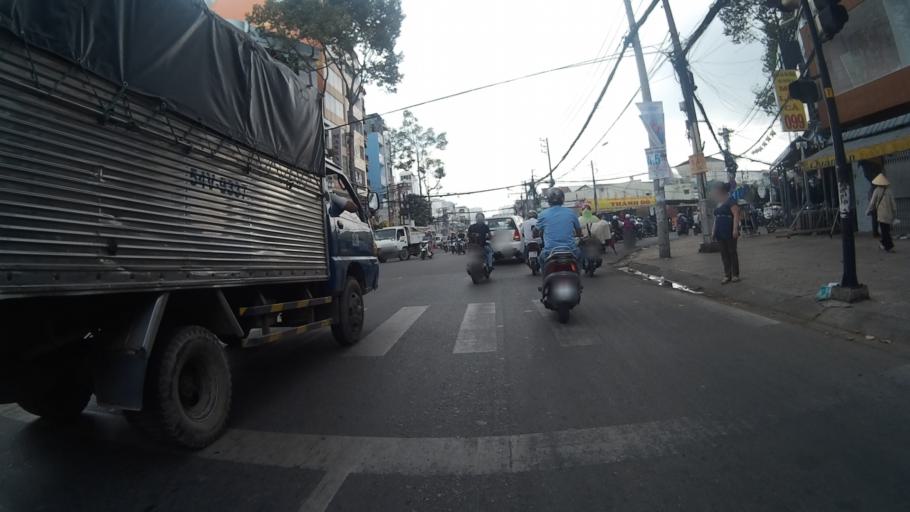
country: VN
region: Ho Chi Minh City
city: Quan Nam
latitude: 10.7544
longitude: 106.6697
